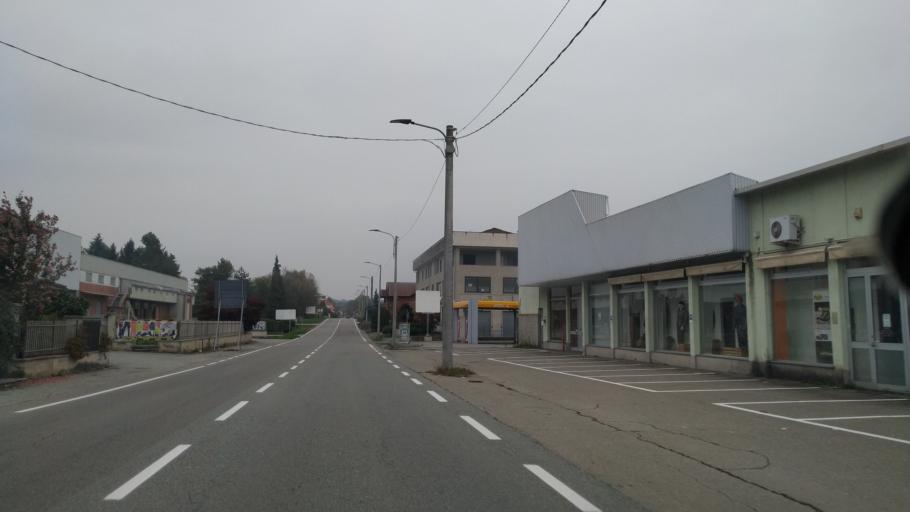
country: IT
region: Piedmont
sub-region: Provincia di Biella
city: Cerreto Castello
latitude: 45.5595
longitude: 8.1721
